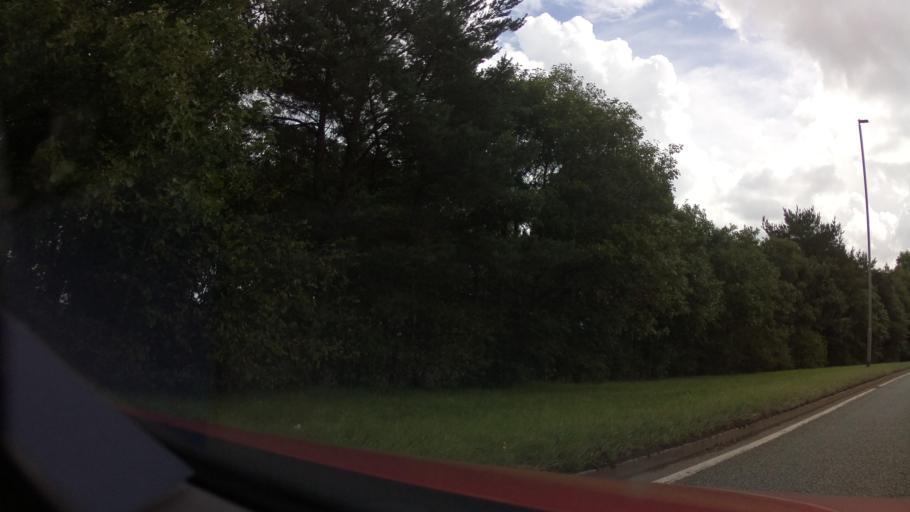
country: GB
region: England
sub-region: Staffordshire
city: Barlaston
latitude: 52.9545
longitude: -2.1922
